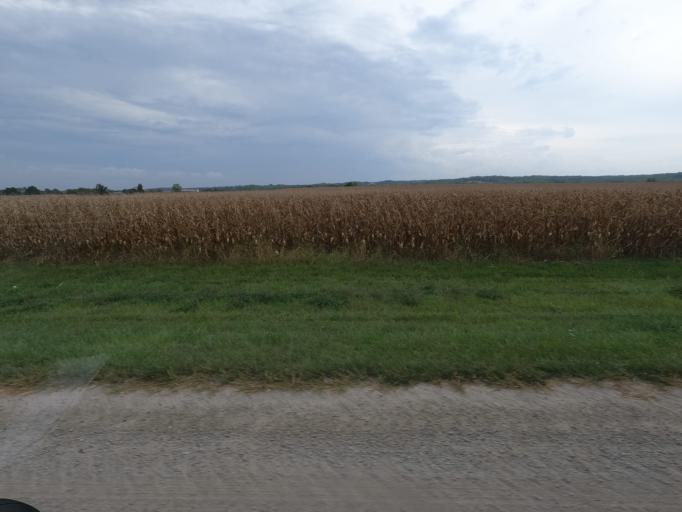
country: US
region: Iowa
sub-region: Van Buren County
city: Keosauqua
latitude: 40.8570
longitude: -92.1081
